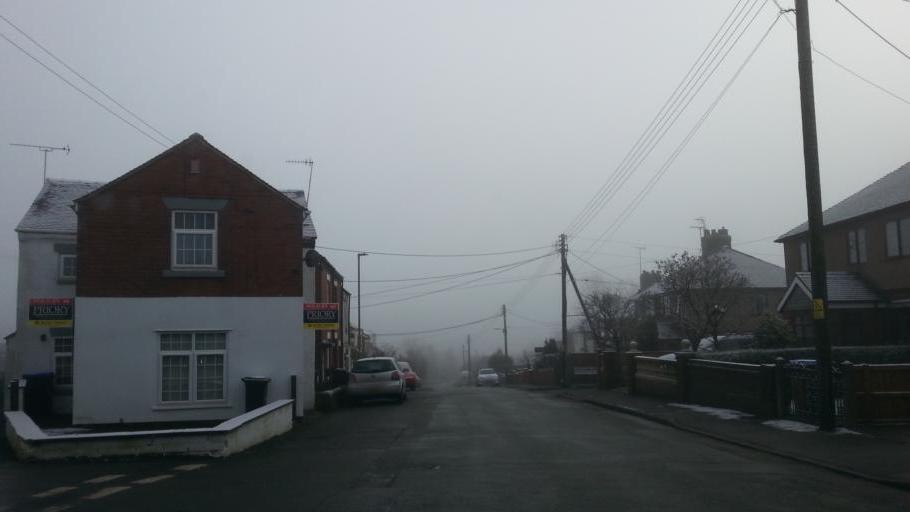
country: GB
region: England
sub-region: Staffordshire
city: Biddulph
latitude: 53.1253
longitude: -2.1784
